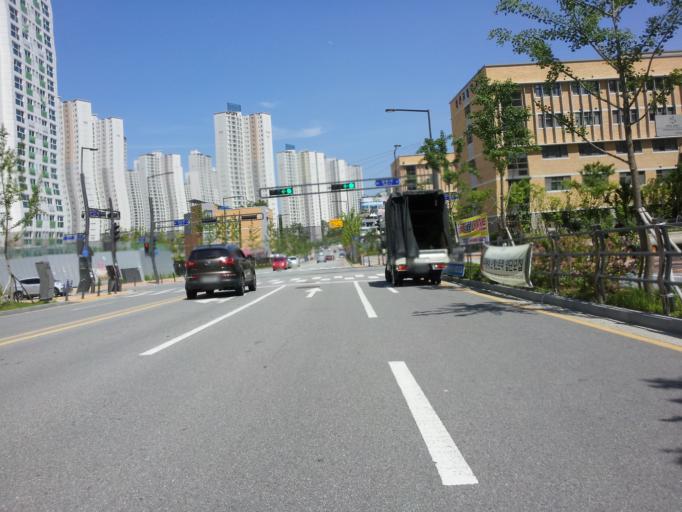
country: KR
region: Chungcheongnam-do
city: Gongju
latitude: 36.5054
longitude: 127.2451
